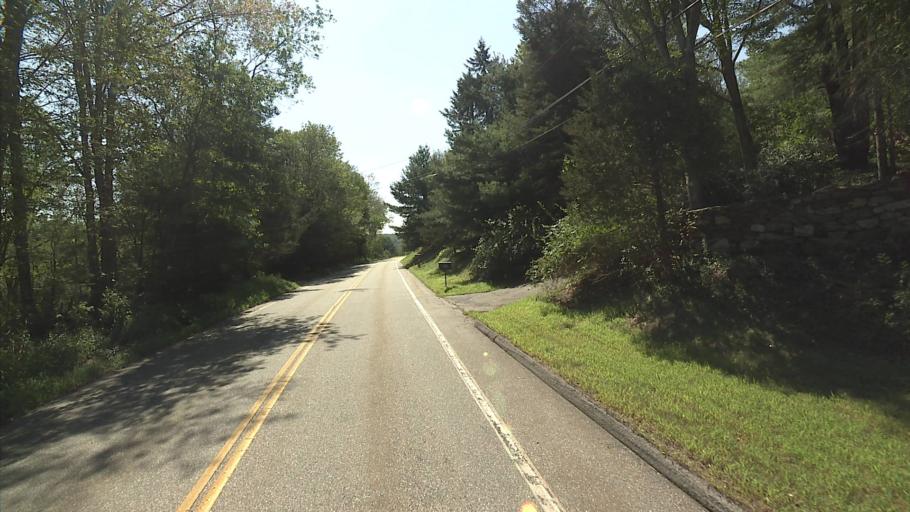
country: US
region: Connecticut
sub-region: Tolland County
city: Storrs
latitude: 41.8175
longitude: -72.1713
